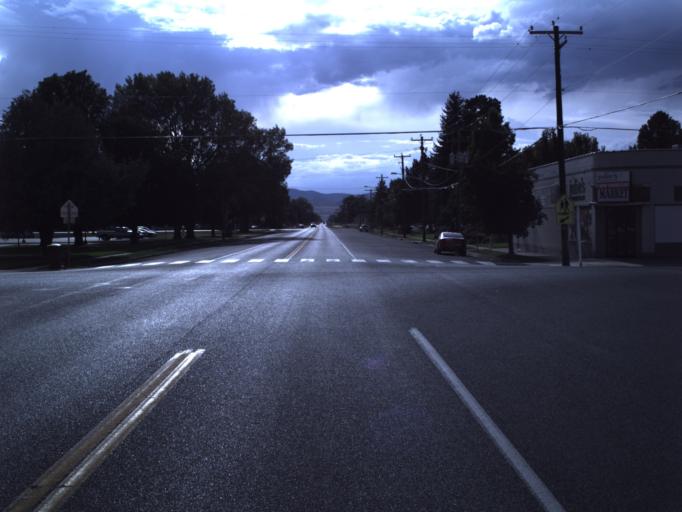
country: US
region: Utah
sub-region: Cache County
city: Lewiston
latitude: 41.9759
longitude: -111.8562
